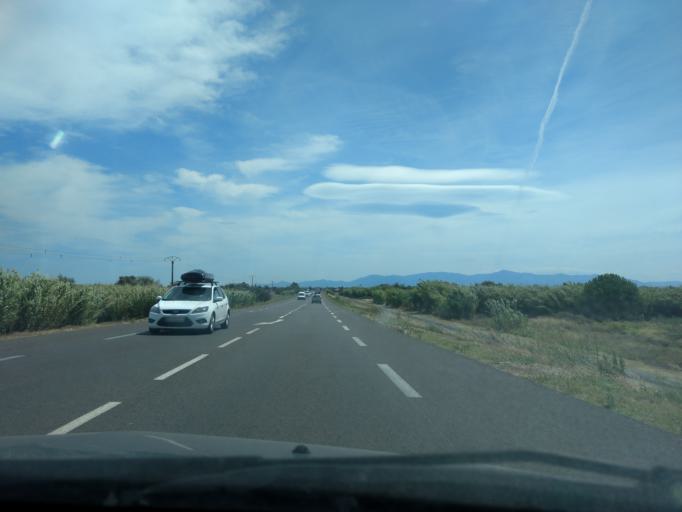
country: FR
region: Languedoc-Roussillon
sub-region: Departement des Pyrenees-Orientales
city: Le Barcares
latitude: 42.7684
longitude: 3.0179
